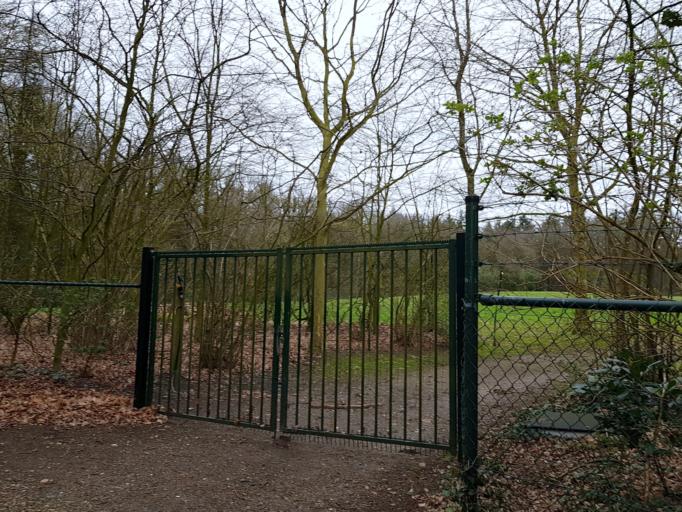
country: NL
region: Gelderland
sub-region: Gemeente Renkum
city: Oosterbeek
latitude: 51.9982
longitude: 5.8407
